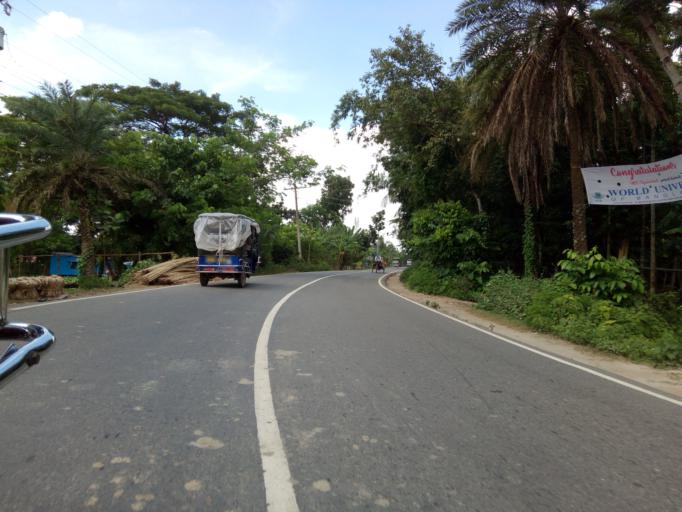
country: BD
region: Dhaka
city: Tungipara
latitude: 22.9802
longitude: 89.8091
